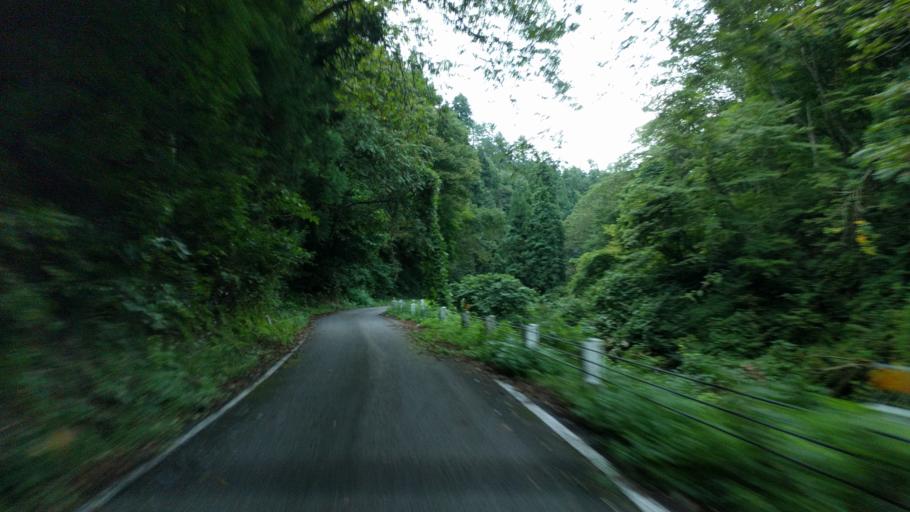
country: JP
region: Fukushima
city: Kitakata
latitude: 37.4660
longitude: 139.7957
